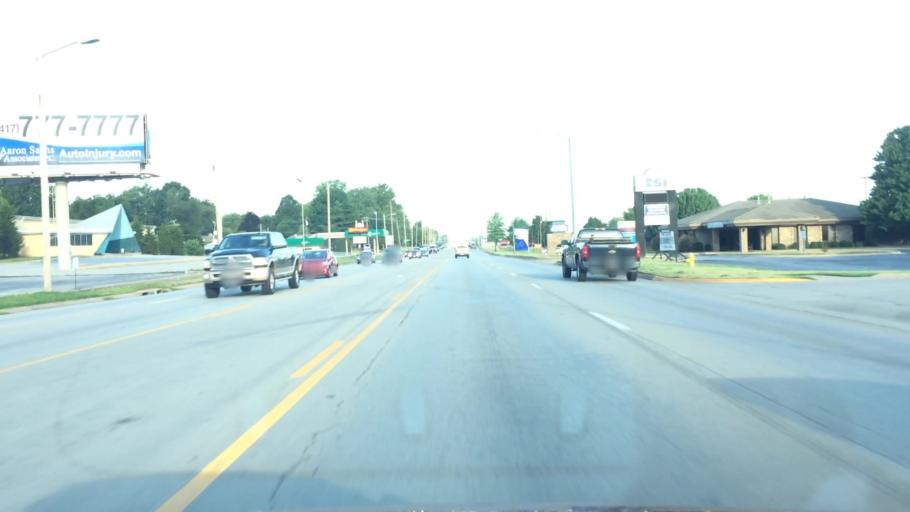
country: US
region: Missouri
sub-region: Greene County
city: Springfield
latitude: 37.1824
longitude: -93.3105
